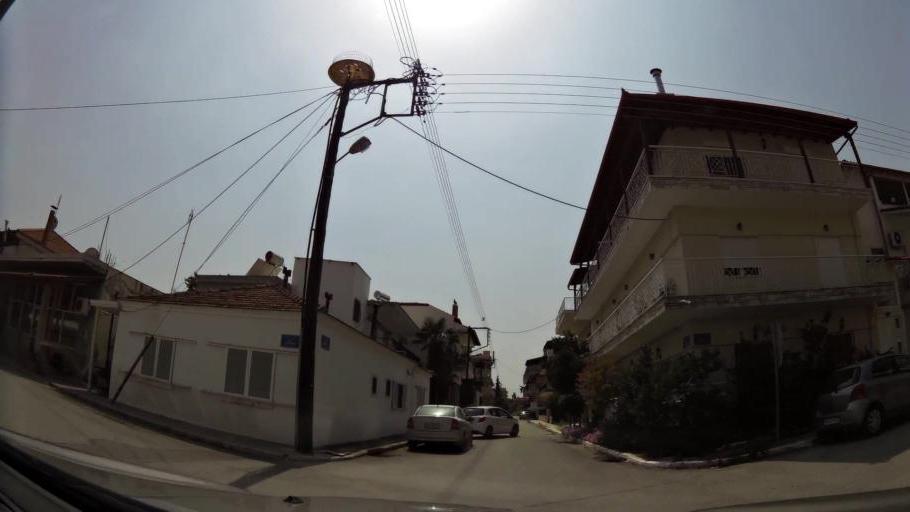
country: GR
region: Central Macedonia
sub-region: Nomos Thessalonikis
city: Nea Magnisia
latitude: 40.6871
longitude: 22.8473
